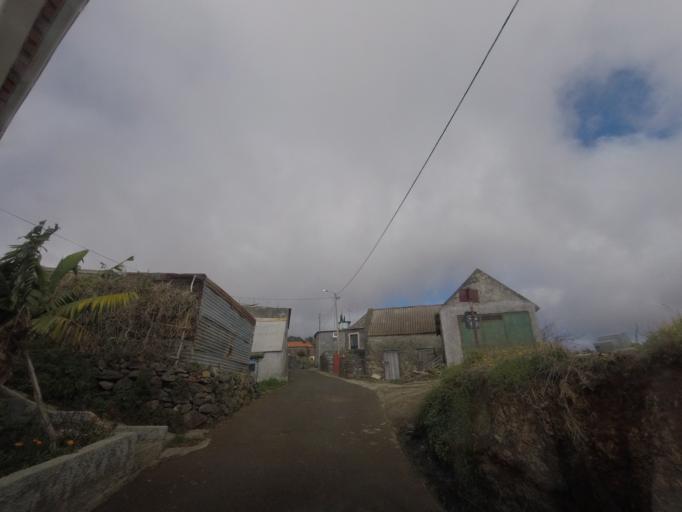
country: PT
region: Madeira
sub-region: Calheta
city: Faja da Ovelha
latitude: 32.7676
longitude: -17.2205
